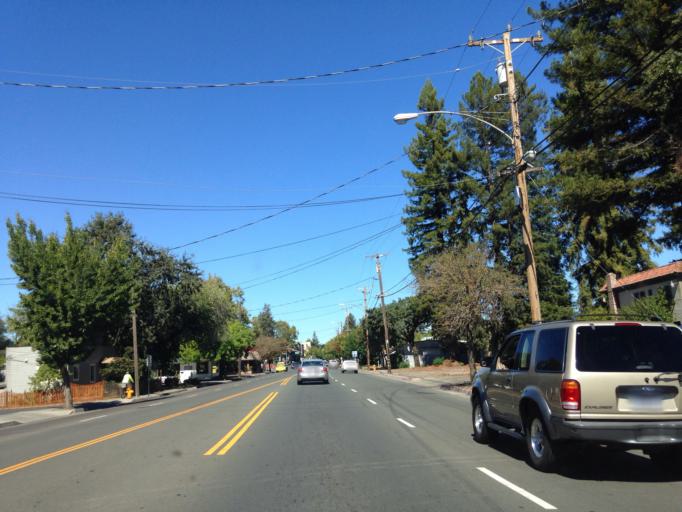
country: US
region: California
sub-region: Sonoma County
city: Healdsburg
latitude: 38.6059
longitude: -122.8689
